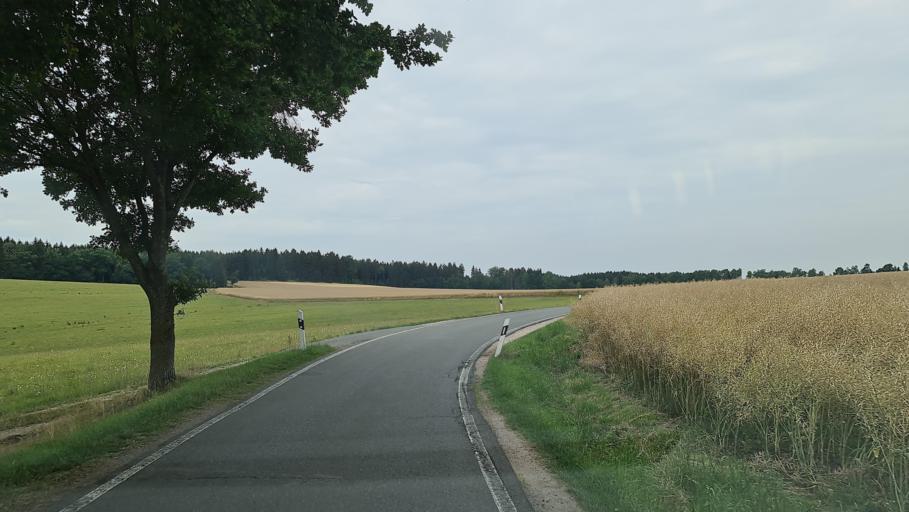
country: DE
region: Saxony
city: Rodewisch
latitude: 50.5662
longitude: 12.4440
